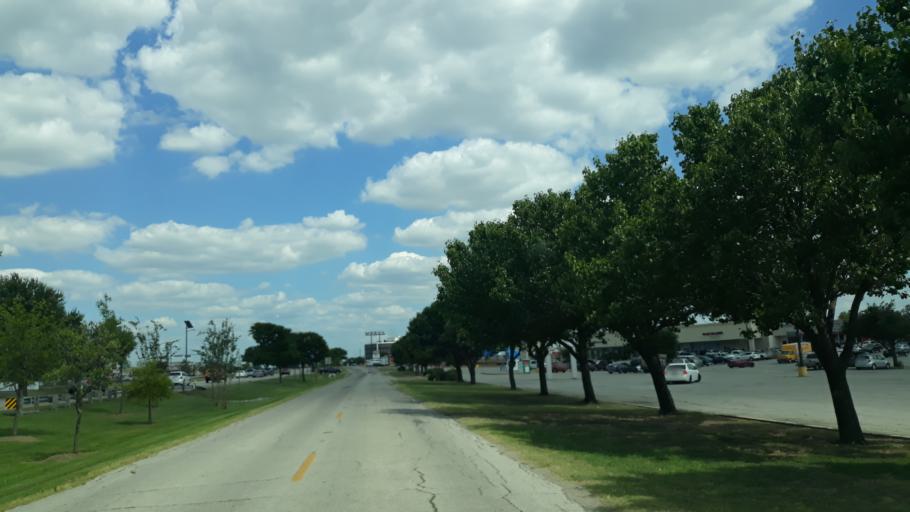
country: US
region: Texas
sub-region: Dallas County
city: Irving
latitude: 32.8310
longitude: -96.9839
